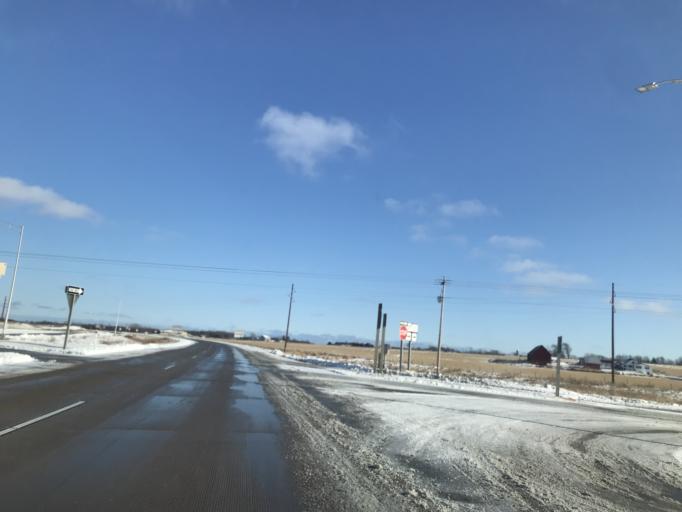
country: US
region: Wisconsin
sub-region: Kewaunee County
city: Luxemburg
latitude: 44.7170
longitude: -87.6211
